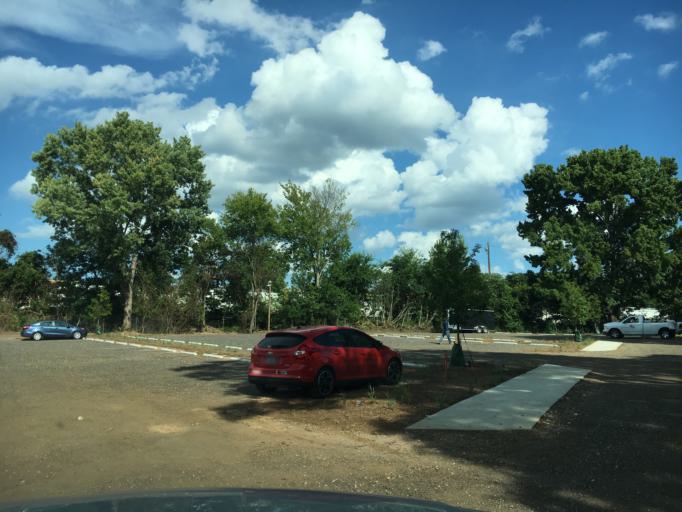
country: US
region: South Carolina
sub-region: Greenville County
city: Sans Souci
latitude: 34.8652
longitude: -82.4155
